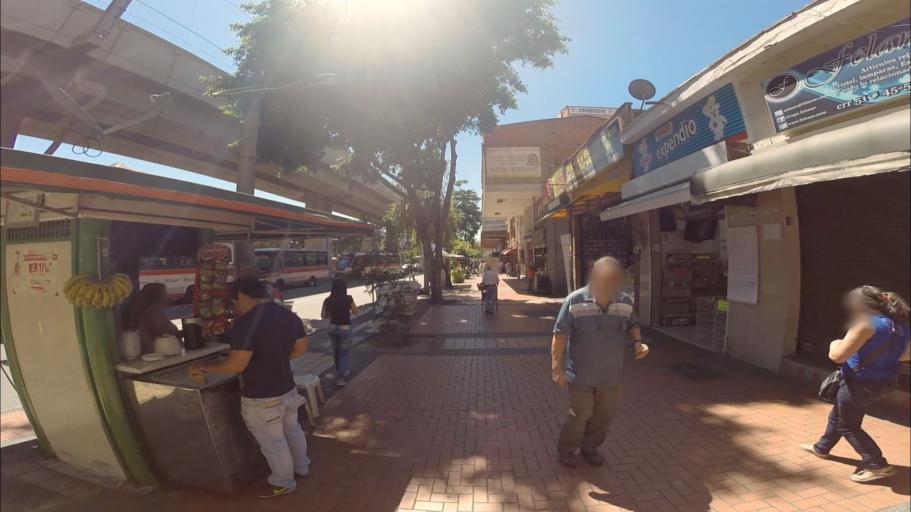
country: CO
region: Antioquia
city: Medellin
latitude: 6.2464
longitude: -75.5701
